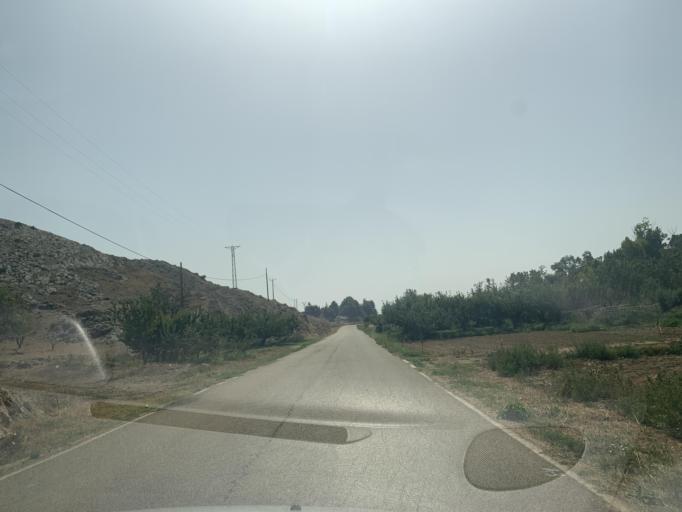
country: ES
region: Aragon
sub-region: Provincia de Zaragoza
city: Almonacid de la Cuba
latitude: 41.2745
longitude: -0.7875
